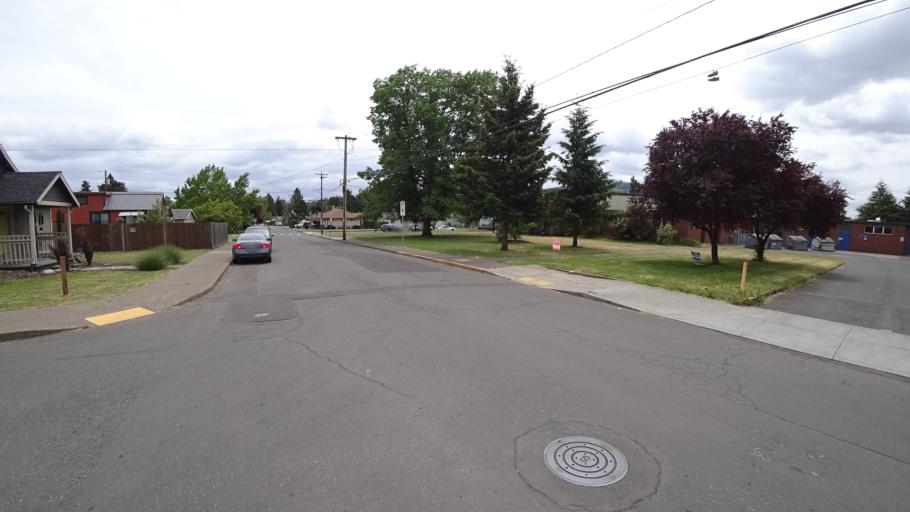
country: US
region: Oregon
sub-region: Multnomah County
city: Lents
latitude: 45.4734
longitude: -122.5707
